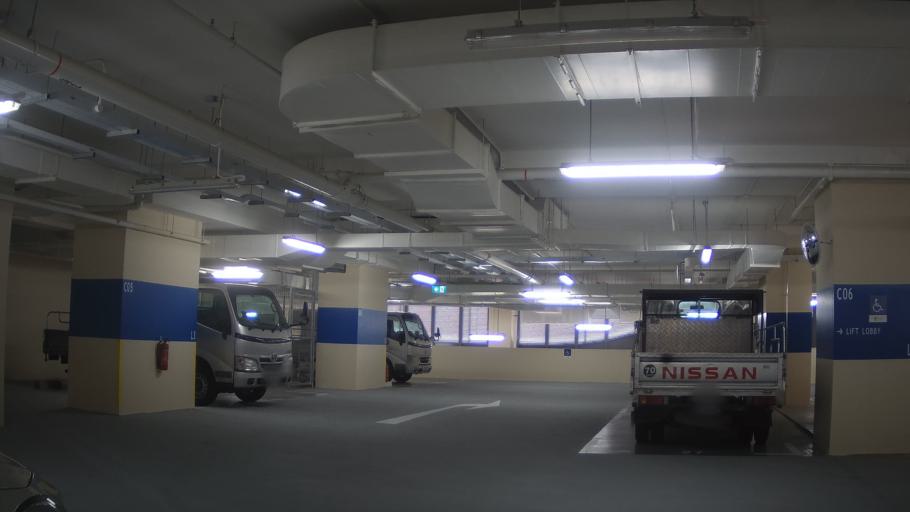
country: SG
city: Singapore
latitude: 1.2816
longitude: 103.8394
